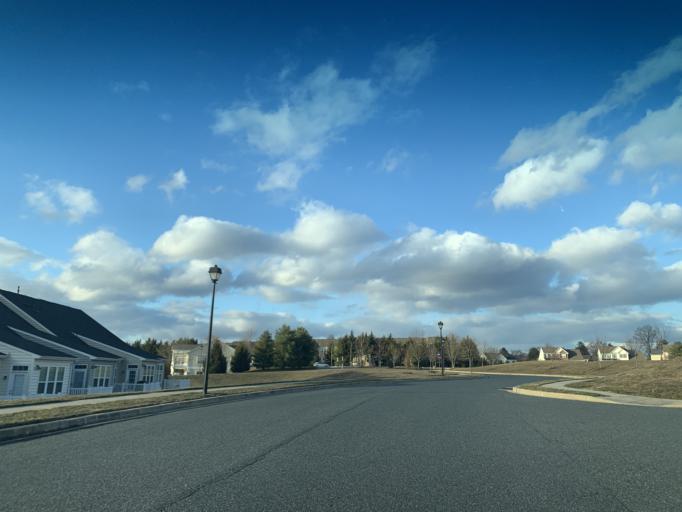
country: US
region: Maryland
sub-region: Harford County
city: South Bel Air
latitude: 39.5359
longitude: -76.3150
